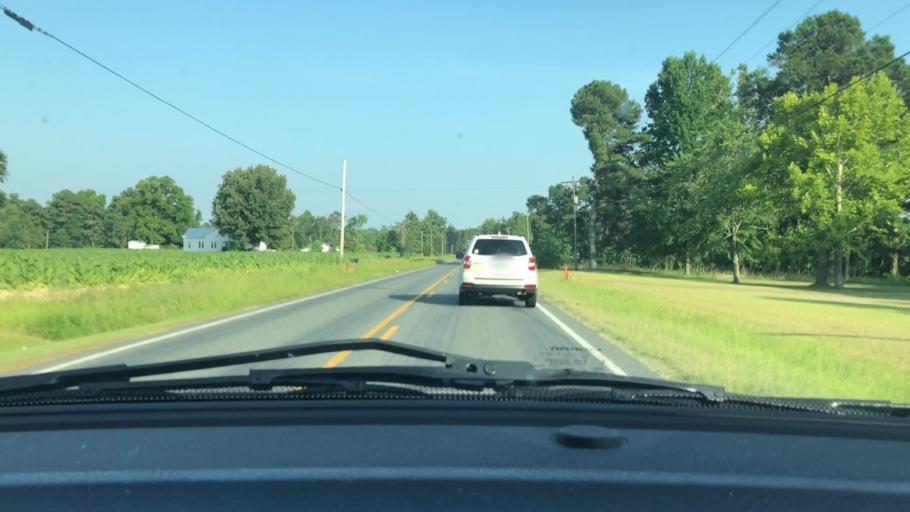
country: US
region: North Carolina
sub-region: Lee County
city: Broadway
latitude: 35.3511
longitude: -79.0732
